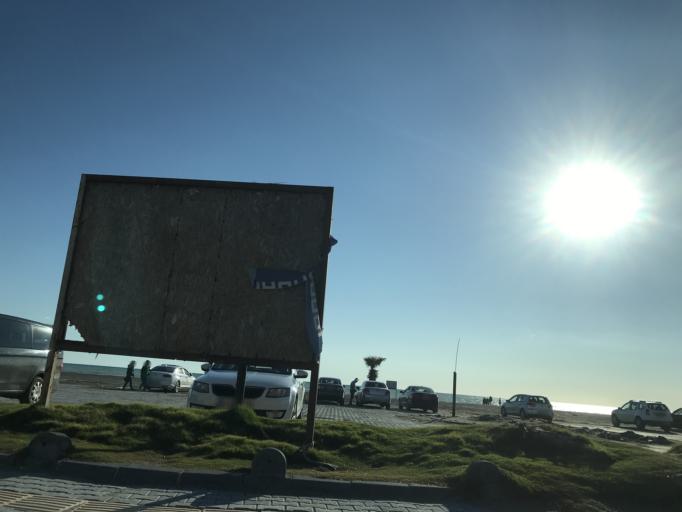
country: TR
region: Hatay
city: Samandag
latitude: 36.0819
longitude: 35.9460
